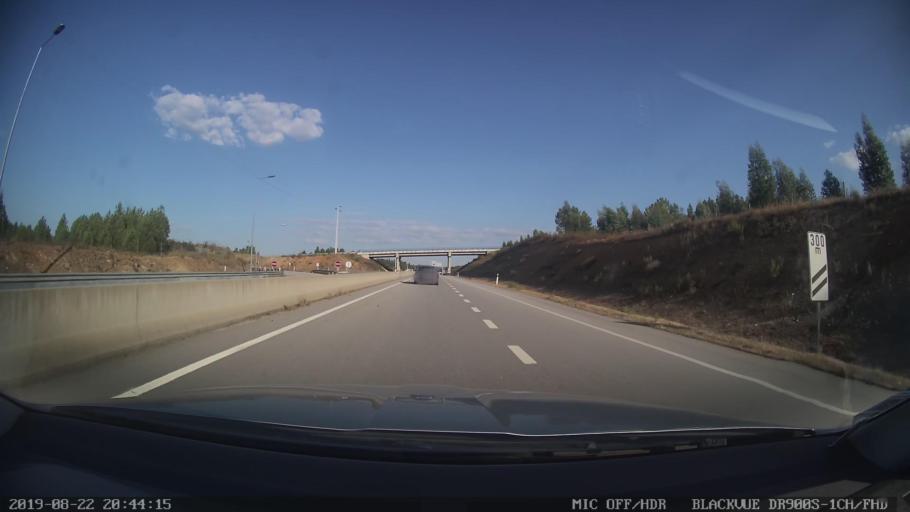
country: PT
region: Castelo Branco
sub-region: Proenca-A-Nova
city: Proenca-a-Nova
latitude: 39.7057
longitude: -7.8477
